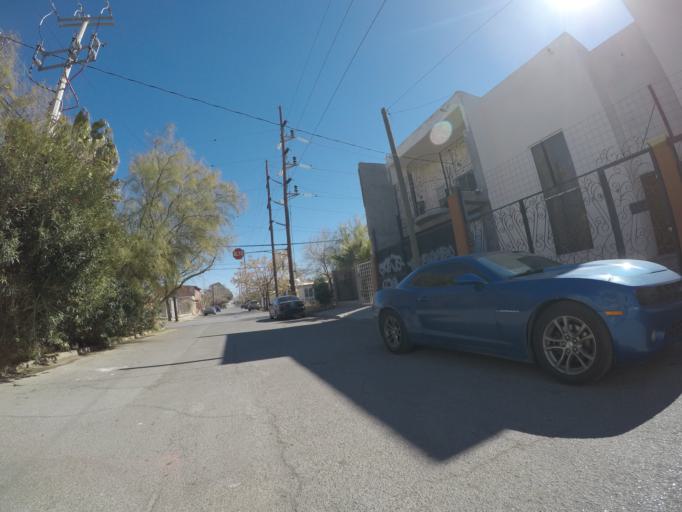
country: MX
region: Chihuahua
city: Ciudad Juarez
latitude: 31.7319
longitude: -106.4380
